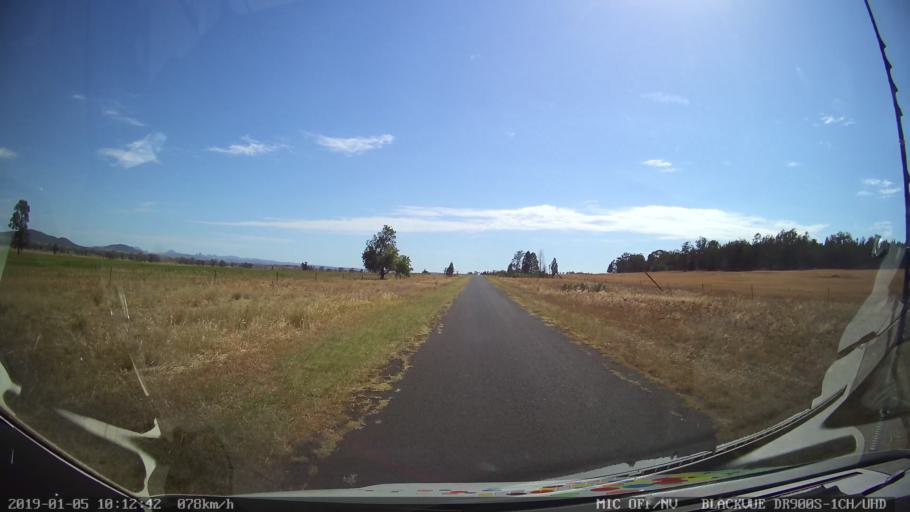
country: AU
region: New South Wales
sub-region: Gilgandra
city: Gilgandra
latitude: -31.6060
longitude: 148.9159
